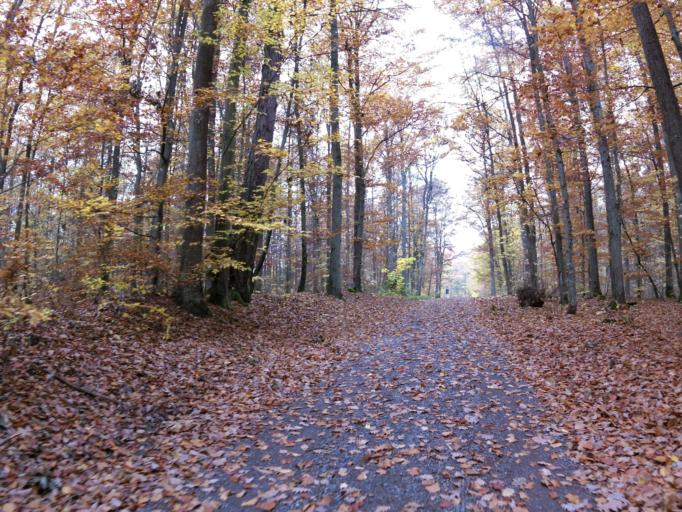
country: DE
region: Bavaria
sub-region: Regierungsbezirk Unterfranken
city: Kist
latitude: 49.7278
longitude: 9.8328
